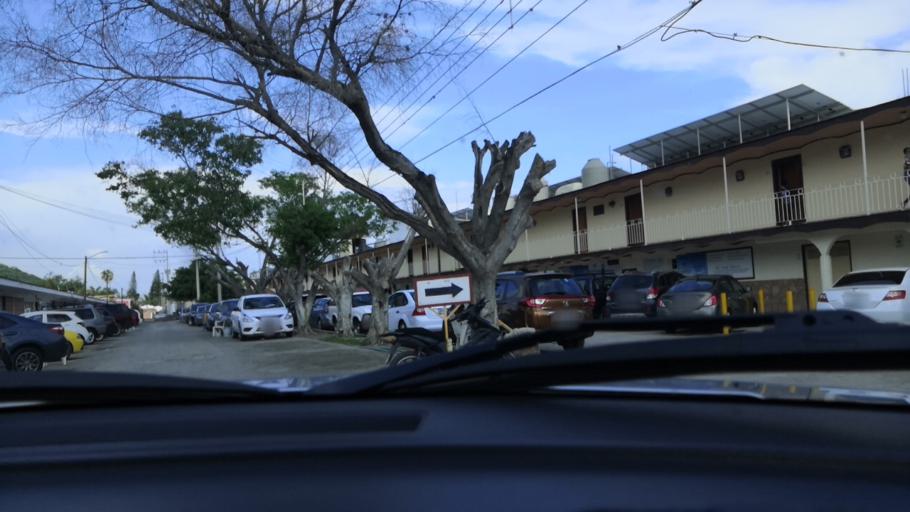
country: MX
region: Jalisco
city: San Juan Cosala
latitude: 20.2848
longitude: -103.3317
